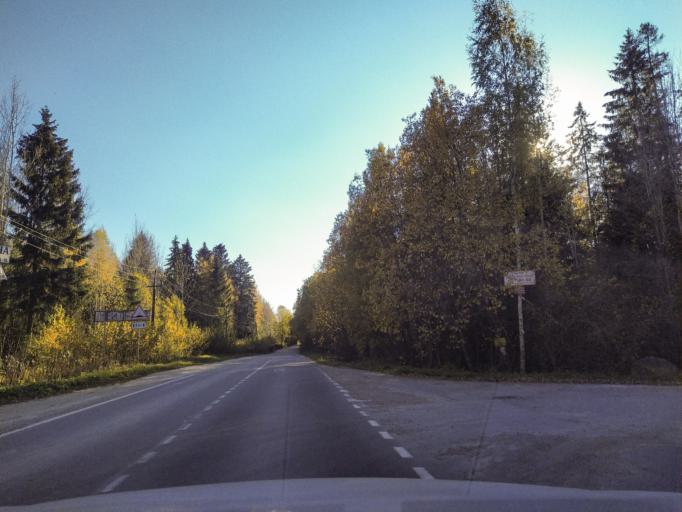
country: RU
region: Leningrad
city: Siverskiy
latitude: 59.3004
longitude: 30.0353
